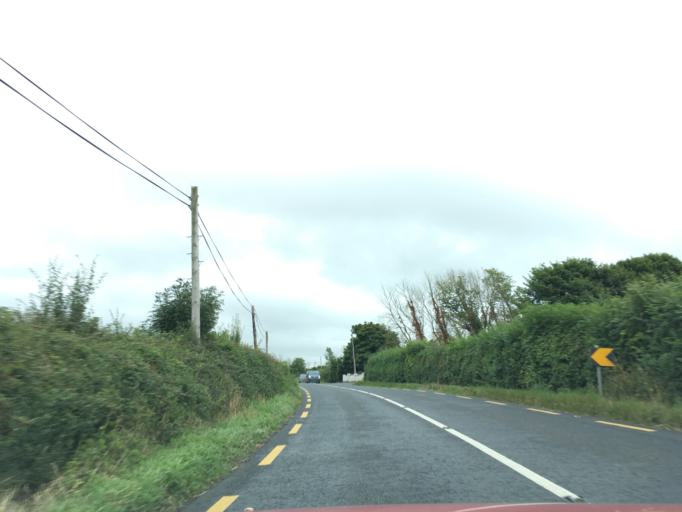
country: IE
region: Munster
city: Fethard
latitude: 52.4202
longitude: -7.7676
